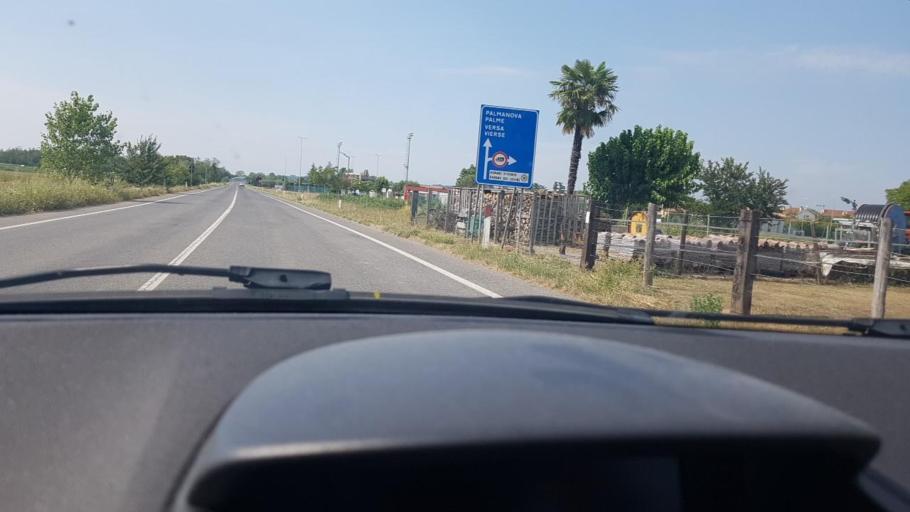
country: IT
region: Friuli Venezia Giulia
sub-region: Provincia di Gorizia
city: Romans d'Isonzo
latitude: 45.8879
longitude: 13.4326
